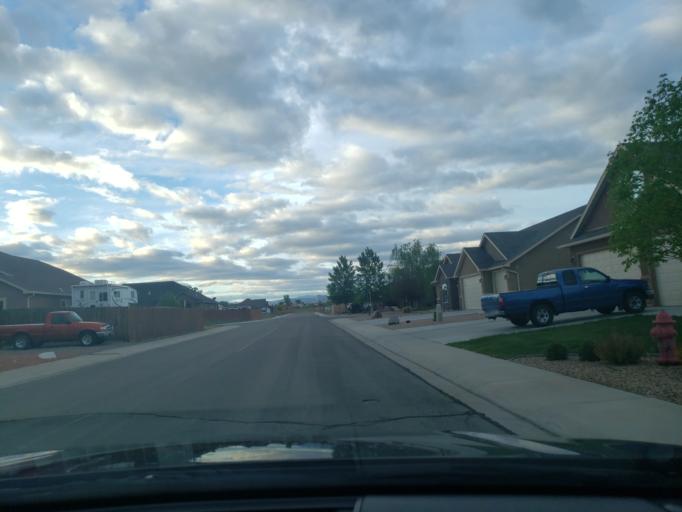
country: US
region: Colorado
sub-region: Mesa County
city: Fruita
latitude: 39.1652
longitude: -108.7081
